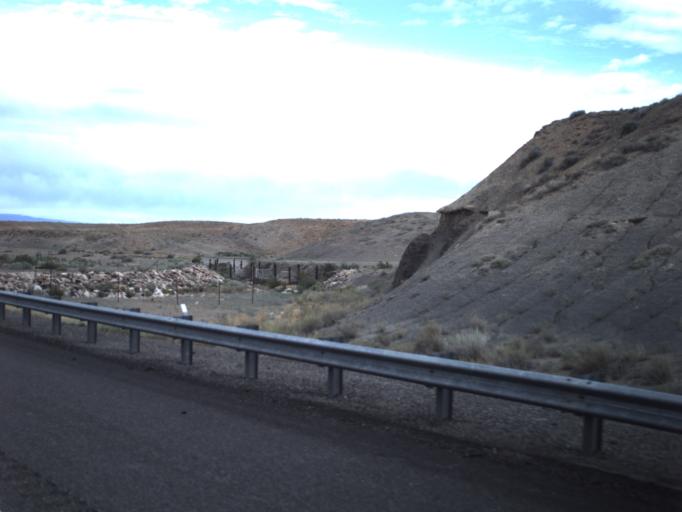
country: US
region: Utah
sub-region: Grand County
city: Moab
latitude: 38.9403
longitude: -109.5230
